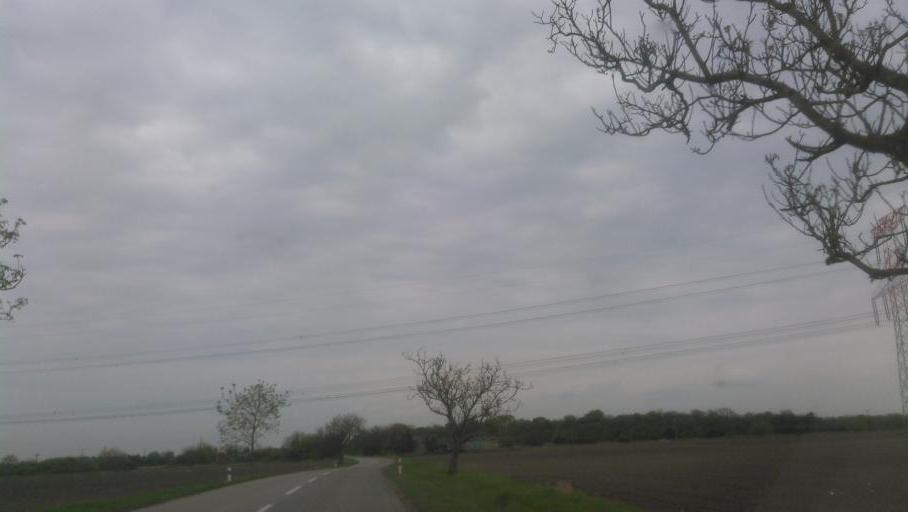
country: SK
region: Bratislavsky
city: Dunajska Luzna
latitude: 48.1370
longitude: 17.3124
